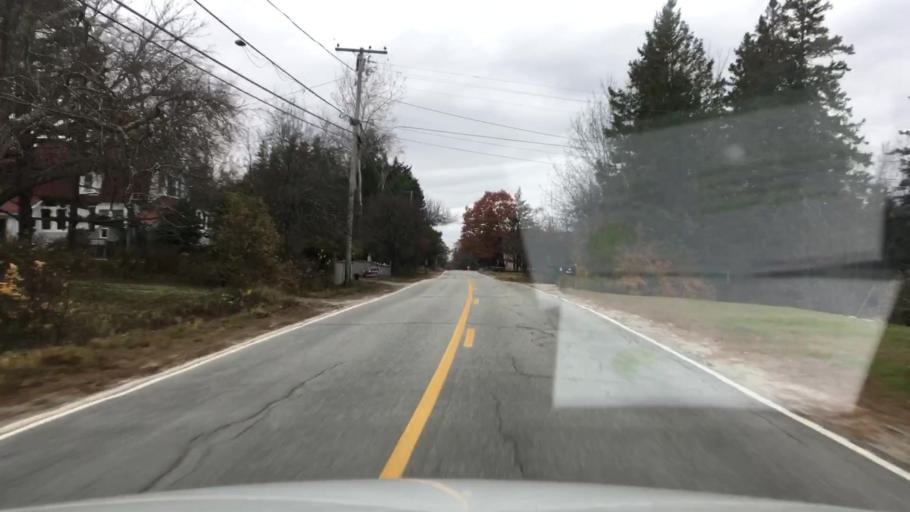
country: US
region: Maine
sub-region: Hancock County
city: Sedgwick
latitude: 44.3616
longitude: -68.5505
